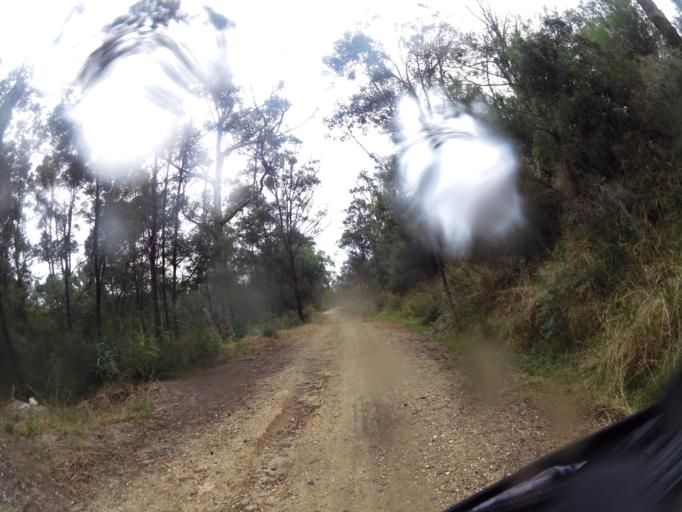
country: AU
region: Victoria
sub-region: East Gippsland
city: Bairnsdale
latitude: -37.7419
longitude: 147.8100
